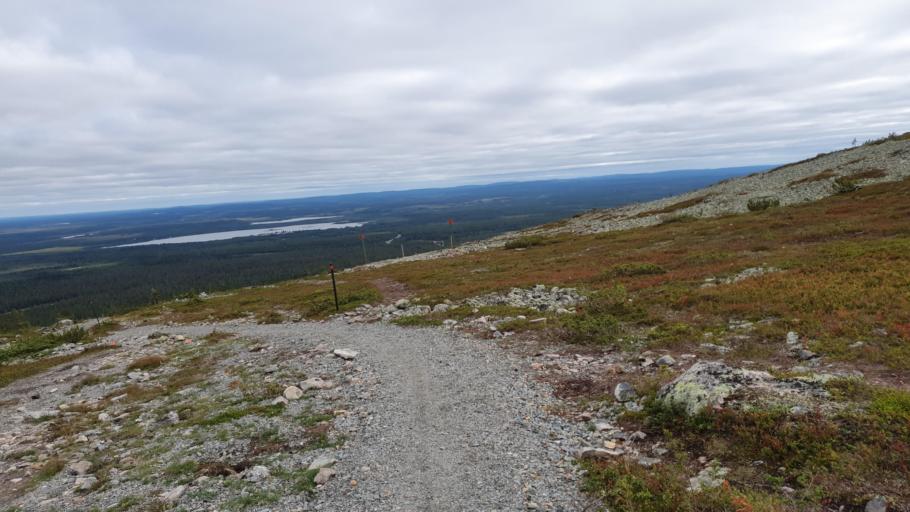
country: FI
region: Lapland
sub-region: Tunturi-Lappi
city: Kolari
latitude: 67.5659
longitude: 24.2499
